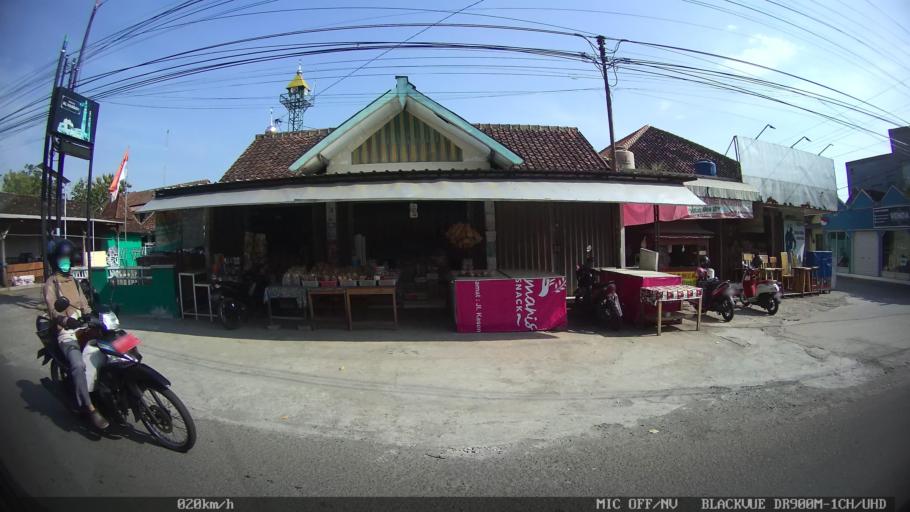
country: ID
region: Daerah Istimewa Yogyakarta
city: Kasihan
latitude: -7.8464
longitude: 110.3385
